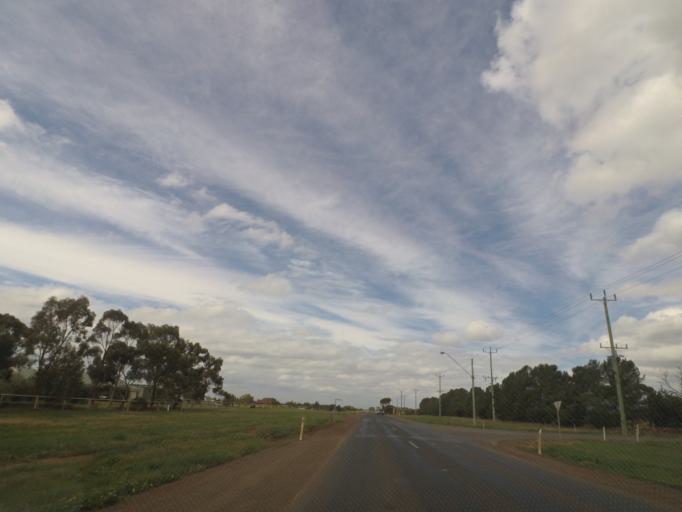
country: AU
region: Victoria
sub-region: Melton
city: Rockbank
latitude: -37.7455
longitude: 144.6303
